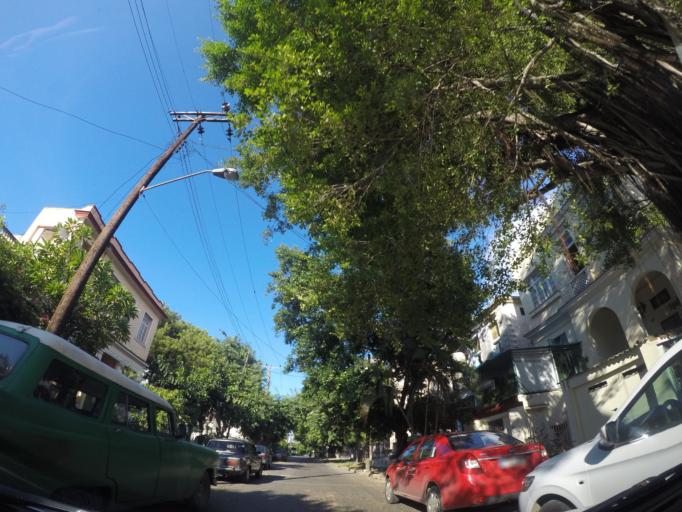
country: CU
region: La Habana
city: Havana
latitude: 23.1369
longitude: -82.3833
